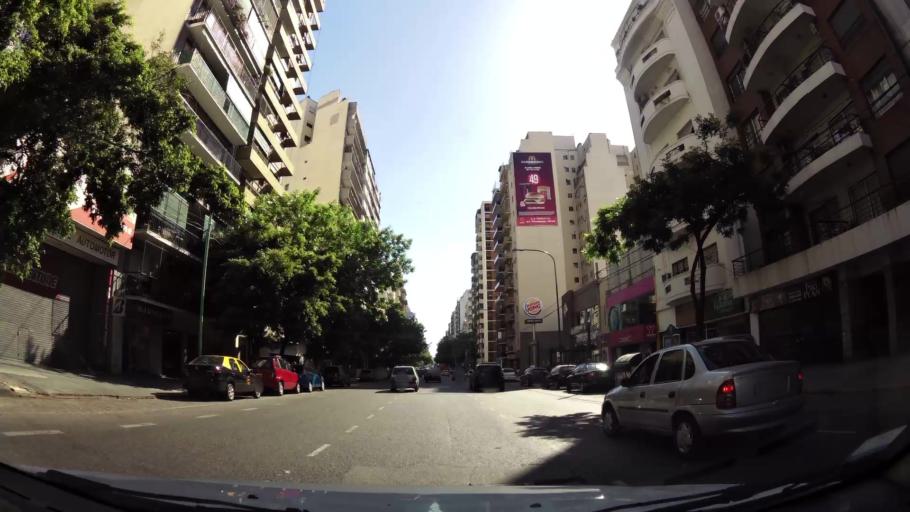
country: AR
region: Buenos Aires F.D.
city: Colegiales
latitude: -34.6140
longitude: -58.4267
